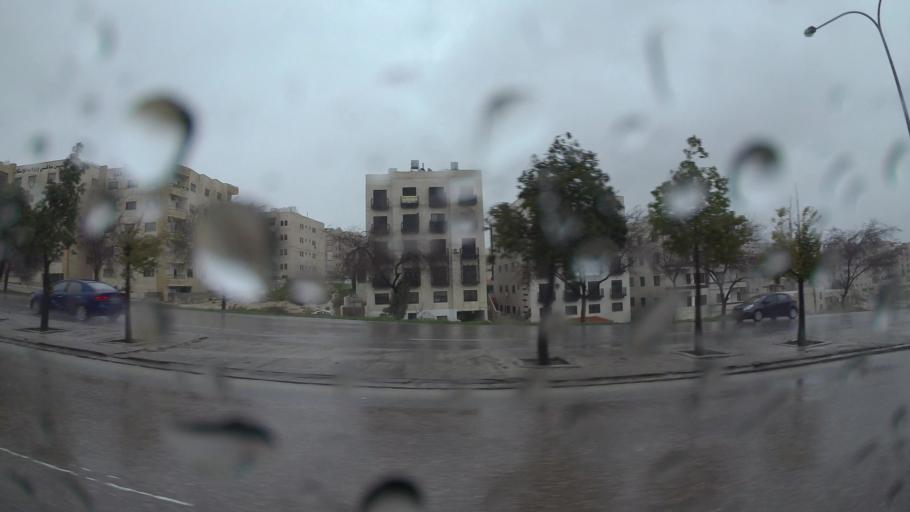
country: JO
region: Amman
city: Al Jubayhah
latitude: 32.0230
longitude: 35.8931
